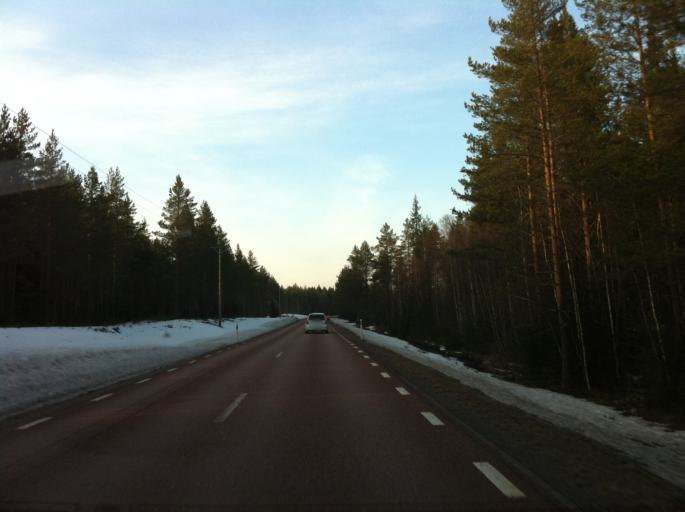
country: SE
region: Vaermland
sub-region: Filipstads Kommun
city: Lesjofors
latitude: 60.1687
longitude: 14.2007
